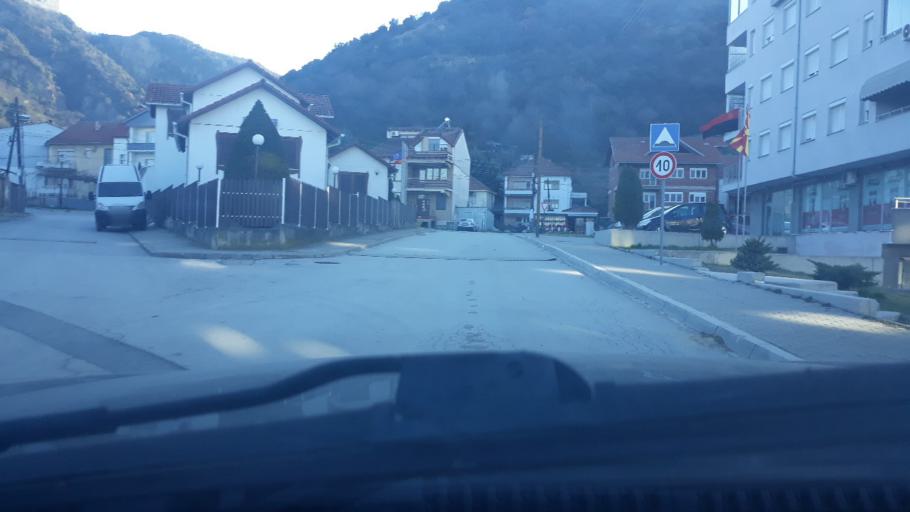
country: MK
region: Strumica
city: Strumica
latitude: 41.4385
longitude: 22.6302
